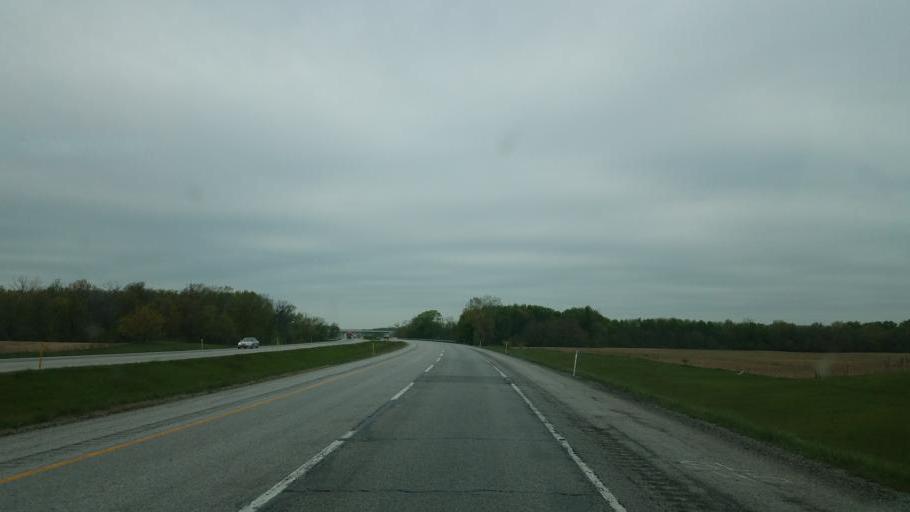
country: US
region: Michigan
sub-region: Saint Joseph County
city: White Pigeon
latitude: 41.7538
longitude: -85.5744
